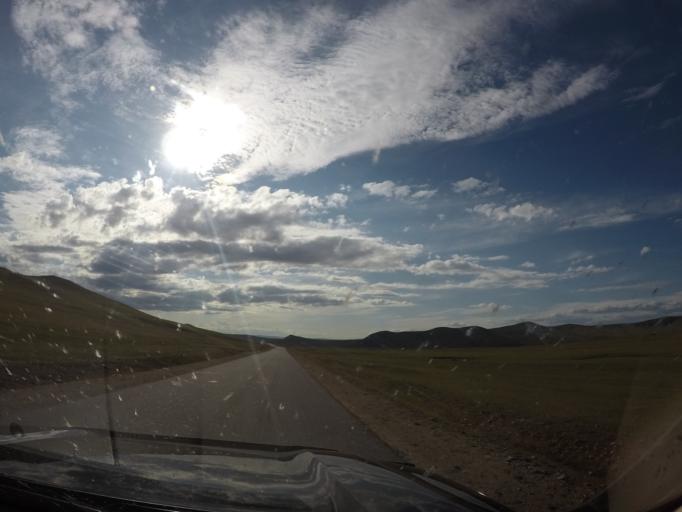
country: MN
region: Central Aimak
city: Bayandelger
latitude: 47.6936
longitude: 108.4980
